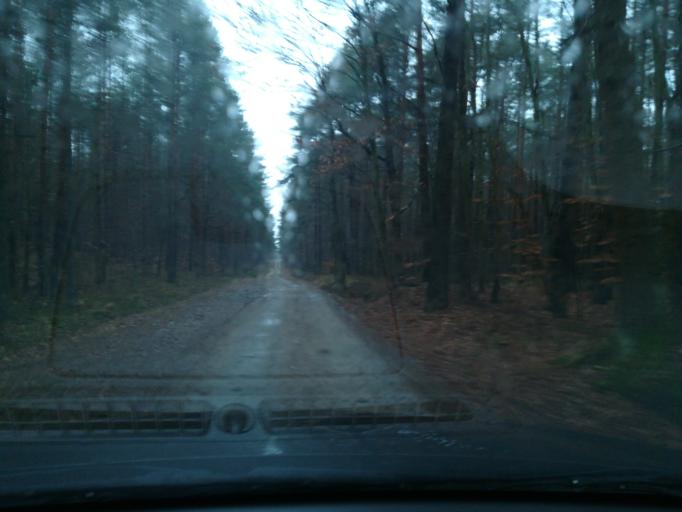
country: PL
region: Subcarpathian Voivodeship
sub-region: Powiat lancucki
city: Bialobrzegi
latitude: 50.1306
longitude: 22.3592
